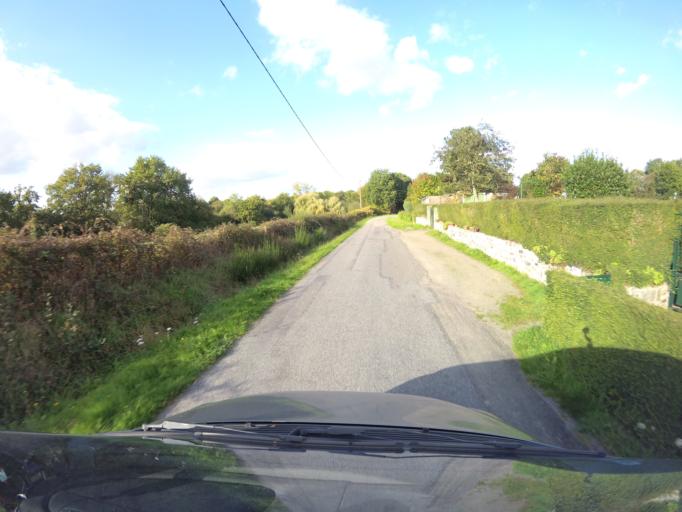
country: FR
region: Brittany
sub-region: Departement du Morbihan
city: Peillac
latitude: 47.7197
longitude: -2.2027
